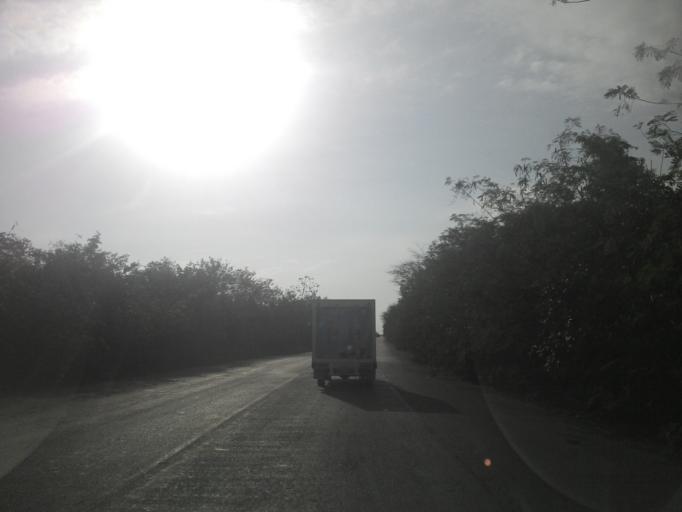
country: MX
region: Yucatan
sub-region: Valladolid
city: Tesoco
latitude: 20.7222
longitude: -88.1796
